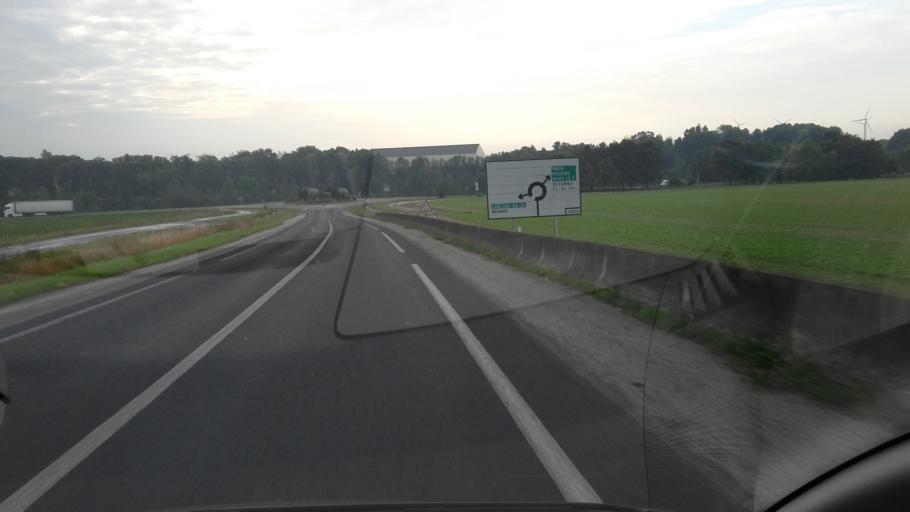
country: FR
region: Champagne-Ardenne
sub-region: Departement de la Marne
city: Fere-Champenoise
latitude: 48.7636
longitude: 3.9986
